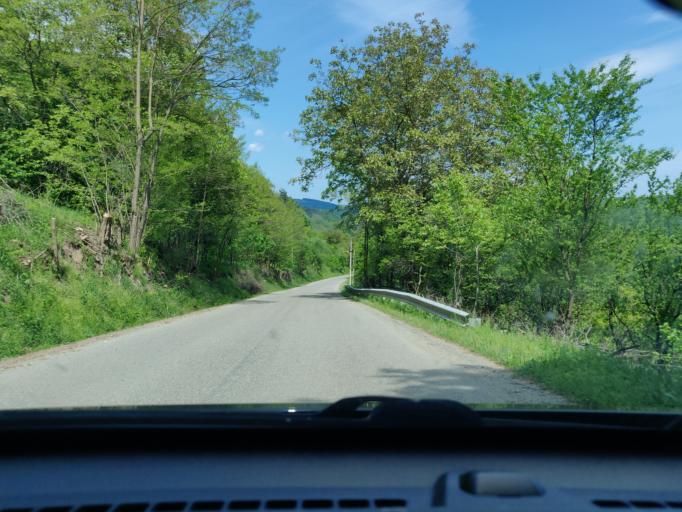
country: RO
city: Vizantea-Manastireasca
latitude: 45.9632
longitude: 26.8204
